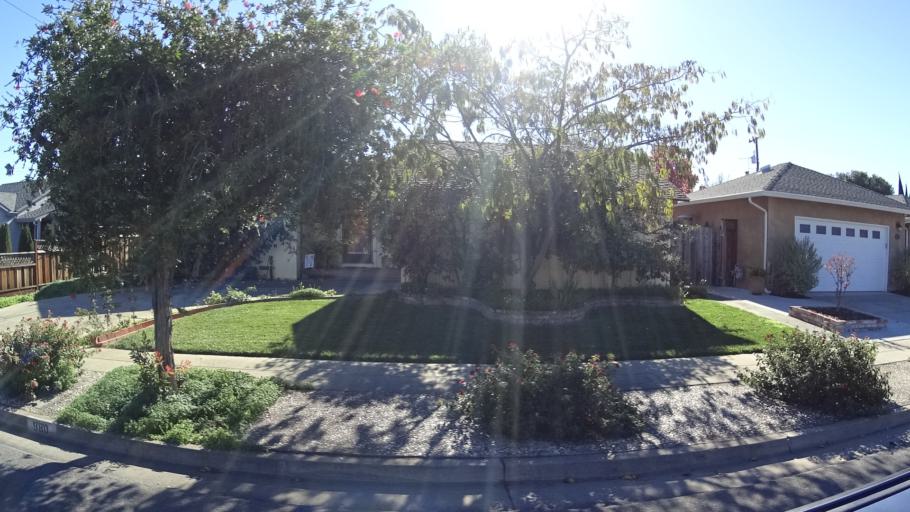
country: US
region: California
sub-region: Santa Clara County
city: Cupertino
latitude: 37.3400
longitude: -122.0082
